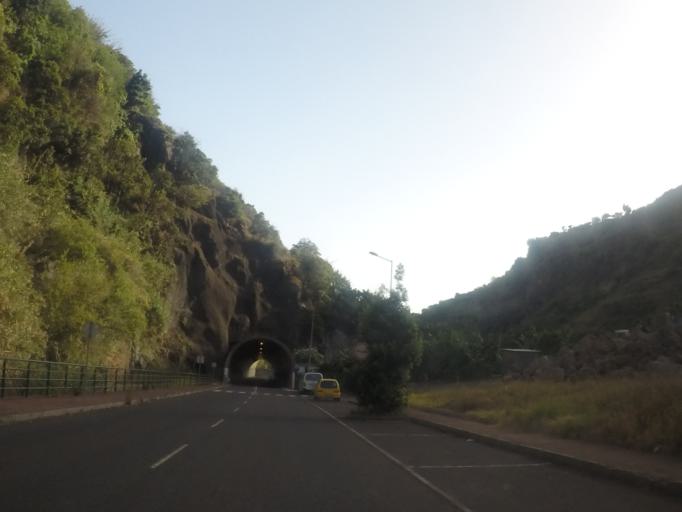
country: PT
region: Madeira
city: Ponta do Sol
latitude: 32.6875
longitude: -17.0972
